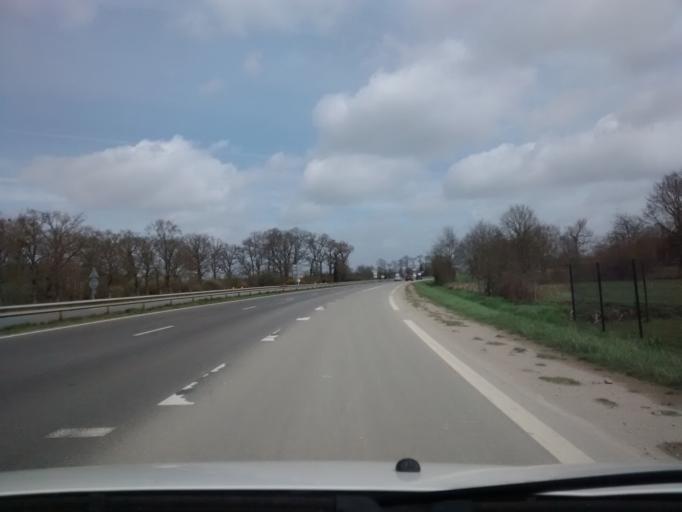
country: FR
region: Brittany
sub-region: Departement d'Ille-et-Vilaine
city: Bruz
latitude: 48.0461
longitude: -1.7536
